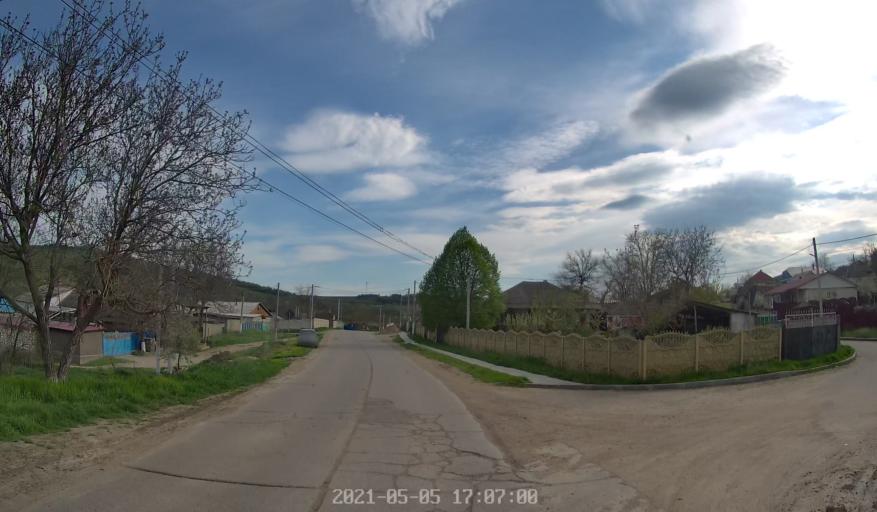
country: MD
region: Chisinau
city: Vadul lui Voda
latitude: 47.0160
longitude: 29.1370
